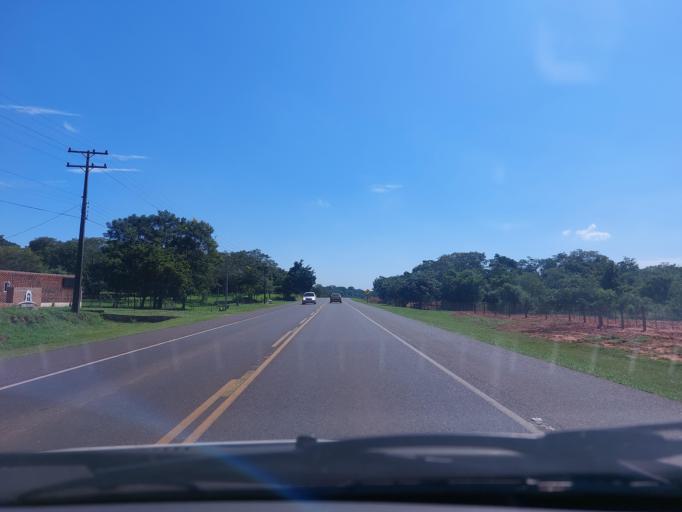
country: PY
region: San Pedro
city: Guayaybi
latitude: -24.6354
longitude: -56.4740
